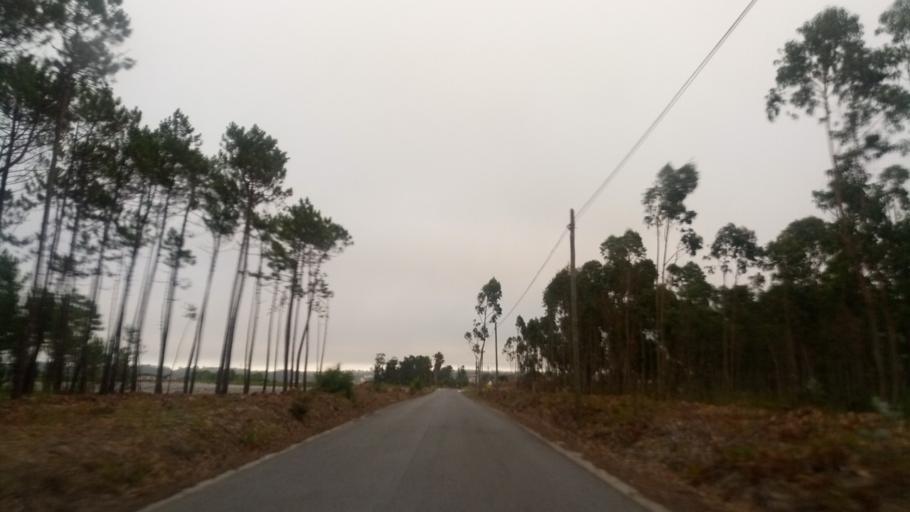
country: PT
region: Leiria
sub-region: Caldas da Rainha
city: Caldas da Rainha
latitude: 39.4415
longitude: -9.1607
